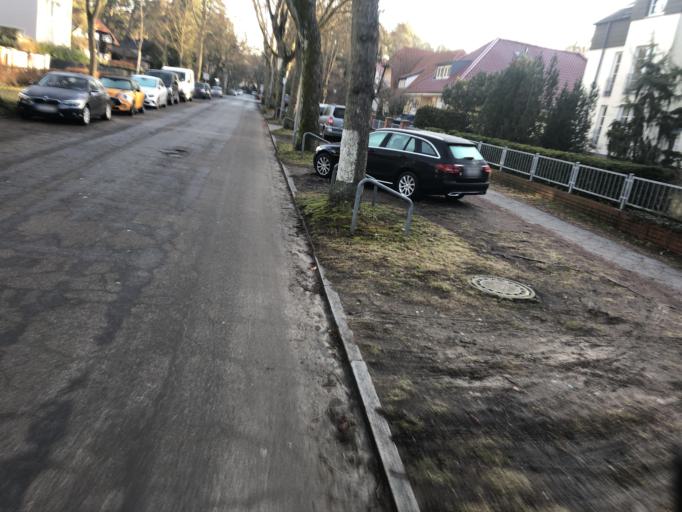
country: DE
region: Berlin
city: Frohnau
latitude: 52.6274
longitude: 13.2834
